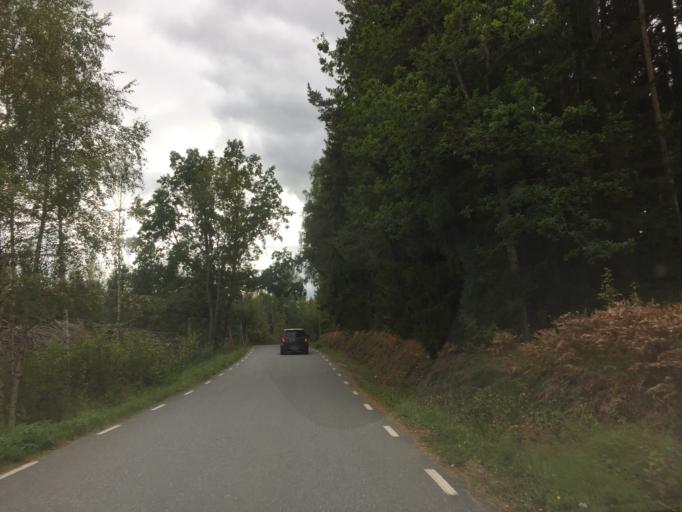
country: SE
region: OErebro
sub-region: Orebro Kommun
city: Hovsta
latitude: 59.3669
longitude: 15.1718
